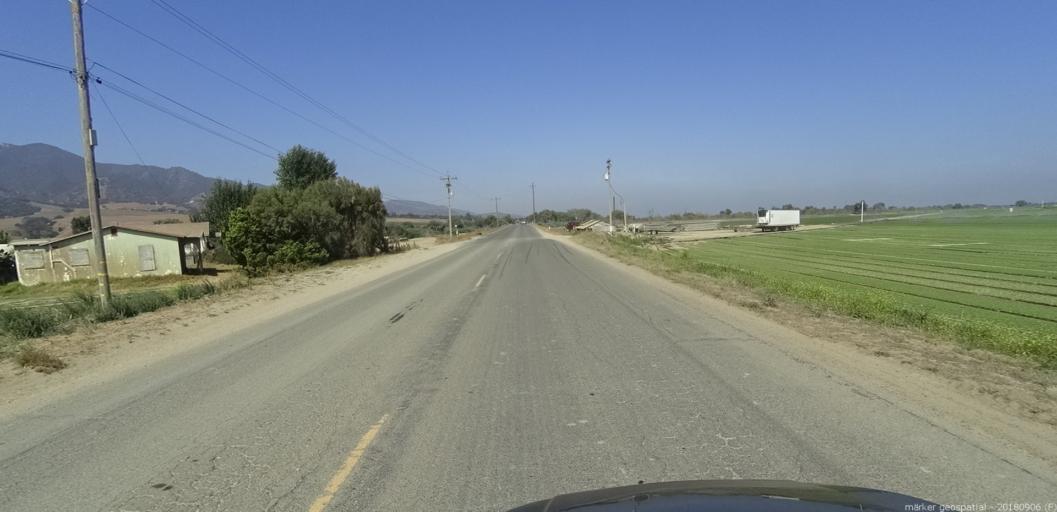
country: US
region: California
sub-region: Monterey County
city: Chualar
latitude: 36.5538
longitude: -121.5437
